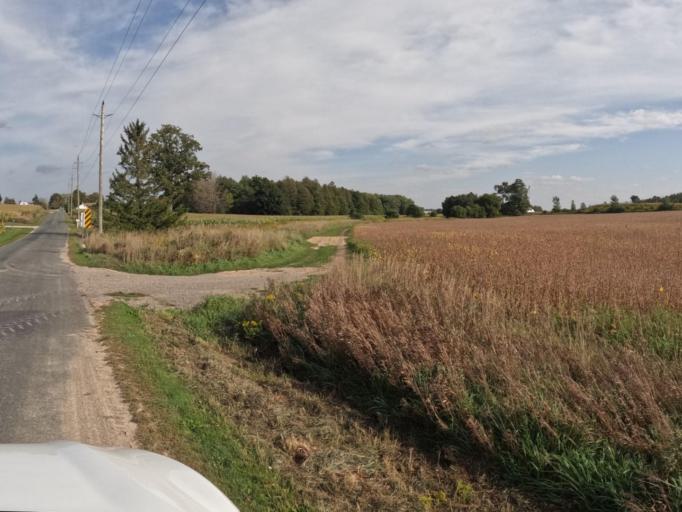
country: CA
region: Ontario
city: Waterloo
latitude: 43.6071
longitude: -80.5478
